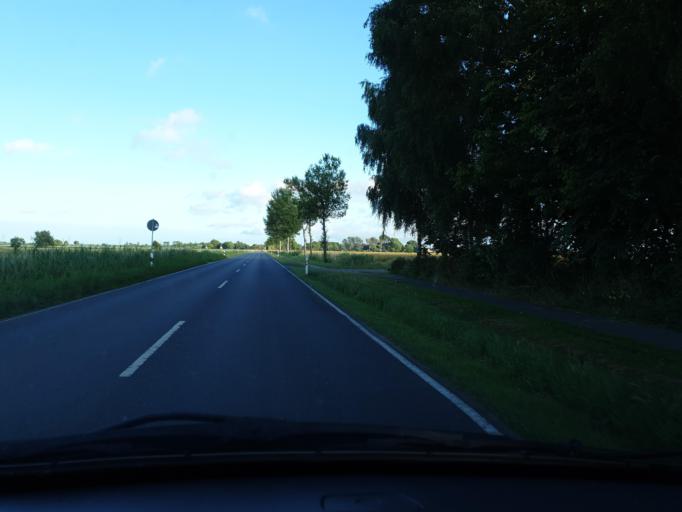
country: DE
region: Schleswig-Holstein
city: Wohrden
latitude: 54.1540
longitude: 9.0147
